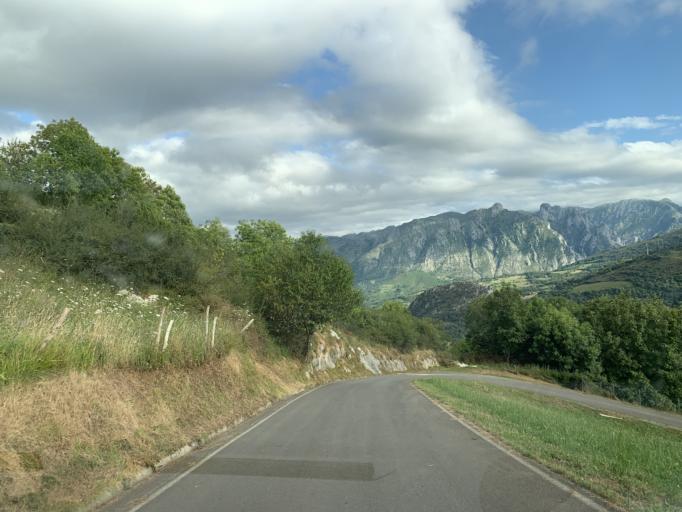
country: ES
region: Asturias
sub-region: Province of Asturias
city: Carrena
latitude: 43.3266
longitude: -4.8600
